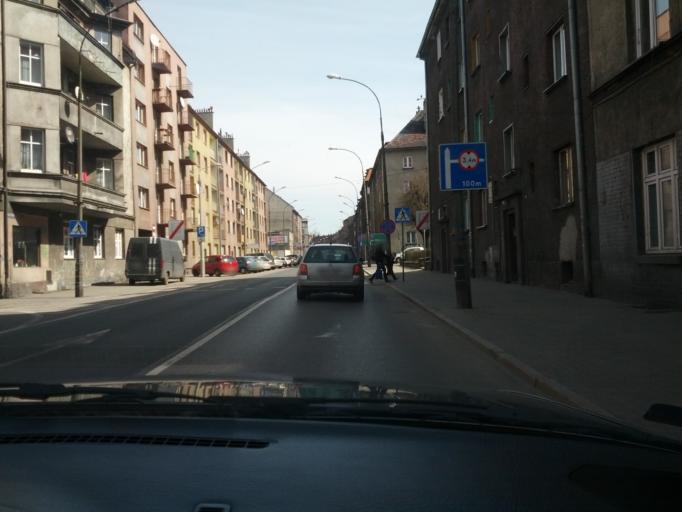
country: PL
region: Silesian Voivodeship
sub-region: Bytom
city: Bytom
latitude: 50.3437
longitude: 18.9235
